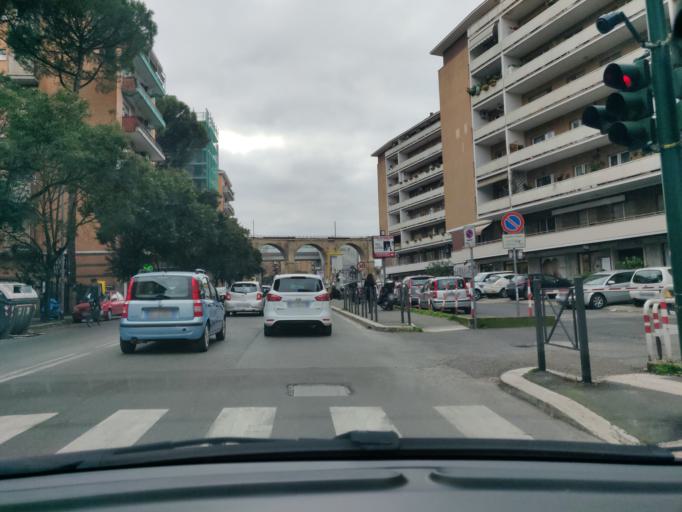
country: VA
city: Vatican City
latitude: 41.9039
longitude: 12.4451
